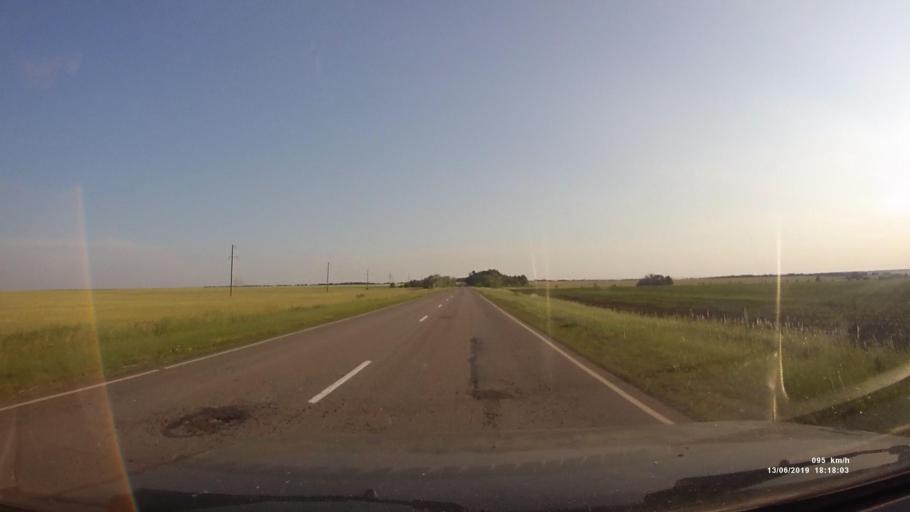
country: RU
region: Rostov
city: Kazanskaya
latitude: 49.9126
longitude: 41.3182
